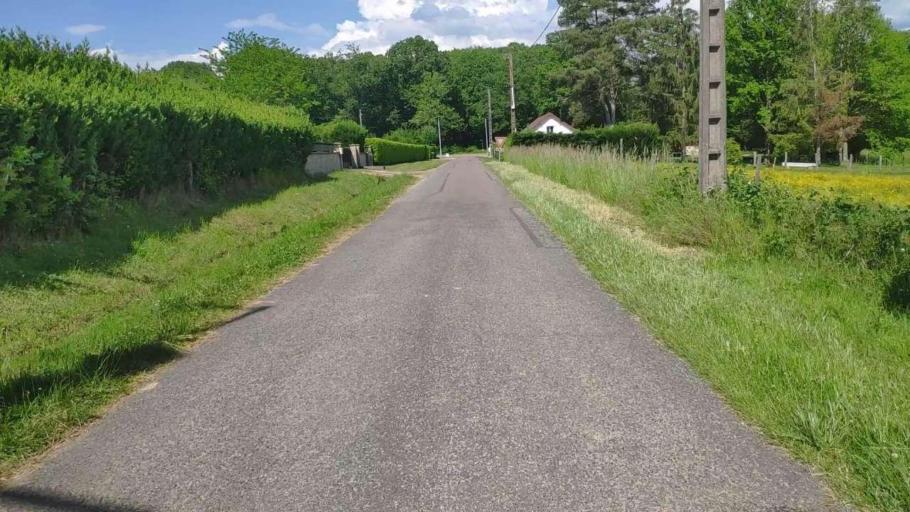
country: FR
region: Franche-Comte
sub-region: Departement du Jura
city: Bletterans
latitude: 46.8039
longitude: 5.4279
